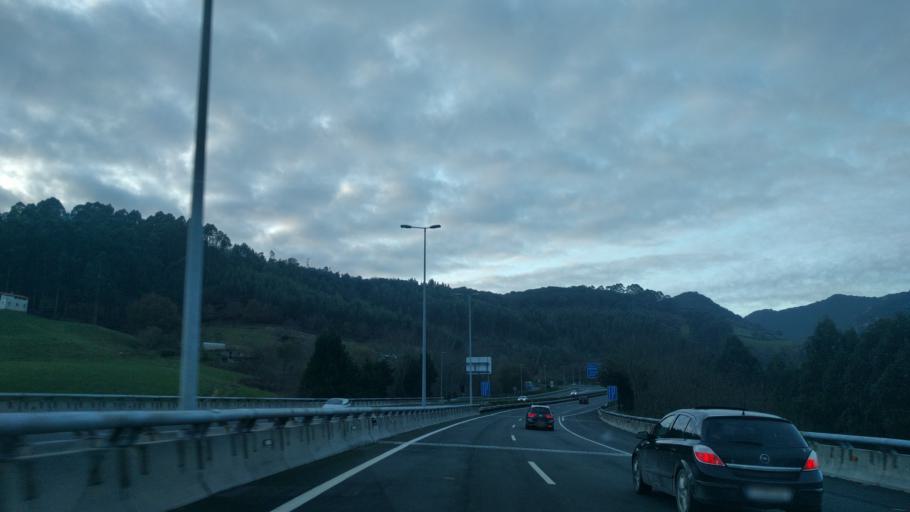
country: ES
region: Cantabria
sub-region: Provincia de Cantabria
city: Liendo
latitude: 43.3846
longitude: -3.3223
